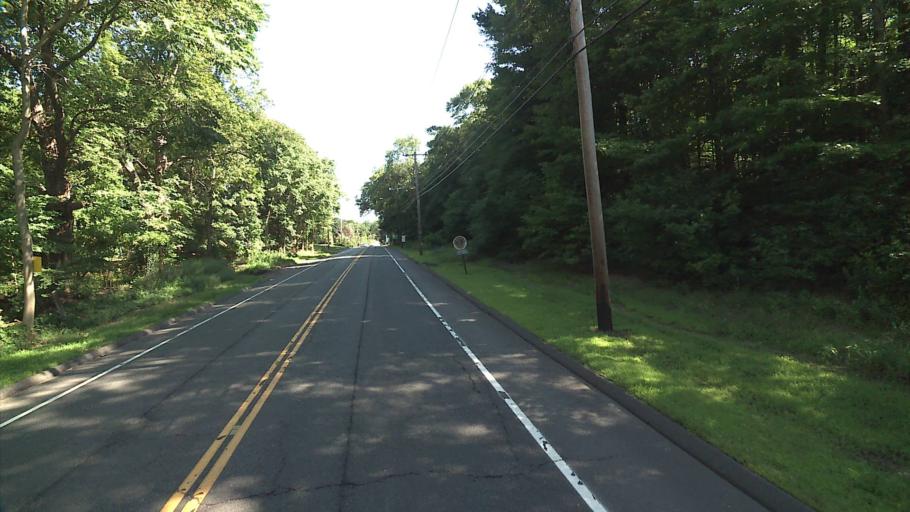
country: US
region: Connecticut
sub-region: New Haven County
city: Cheshire Village
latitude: 41.5610
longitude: -72.8902
